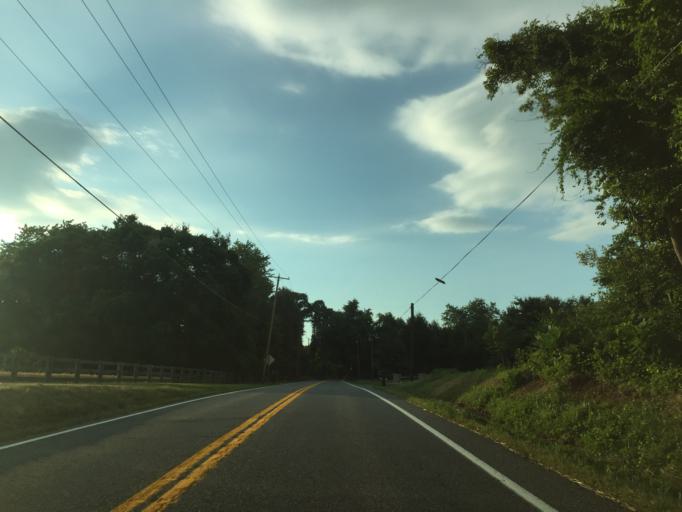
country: US
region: Maryland
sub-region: Harford County
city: Jarrettsville
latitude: 39.6076
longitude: -76.5140
